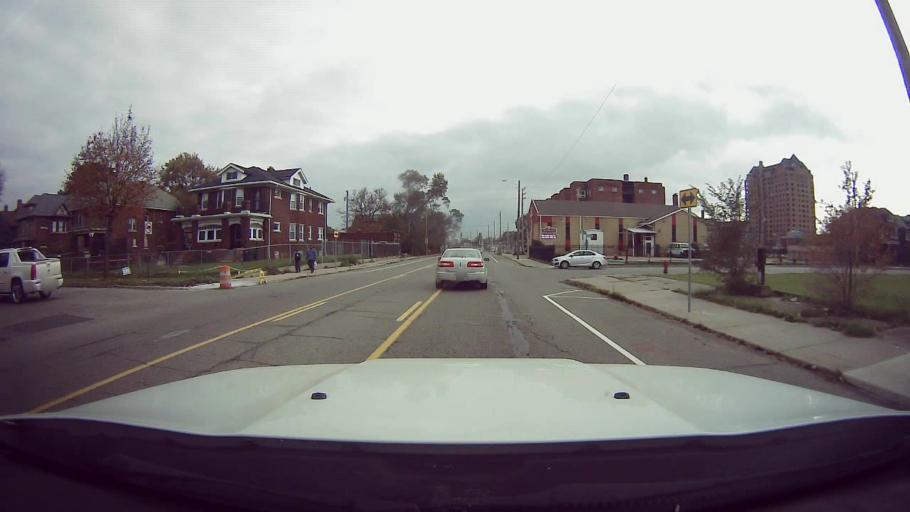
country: US
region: Michigan
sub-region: Wayne County
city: Highland Park
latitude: 42.3616
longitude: -83.1009
